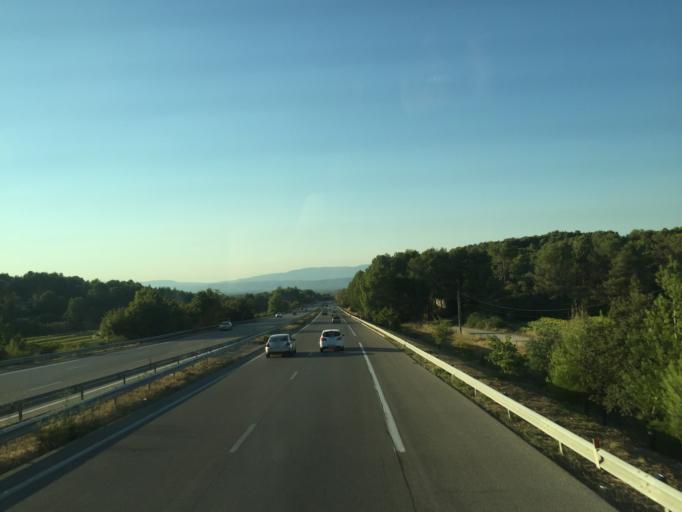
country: FR
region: Provence-Alpes-Cote d'Azur
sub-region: Departement des Bouches-du-Rhone
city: Venelles
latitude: 43.6141
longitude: 5.4970
